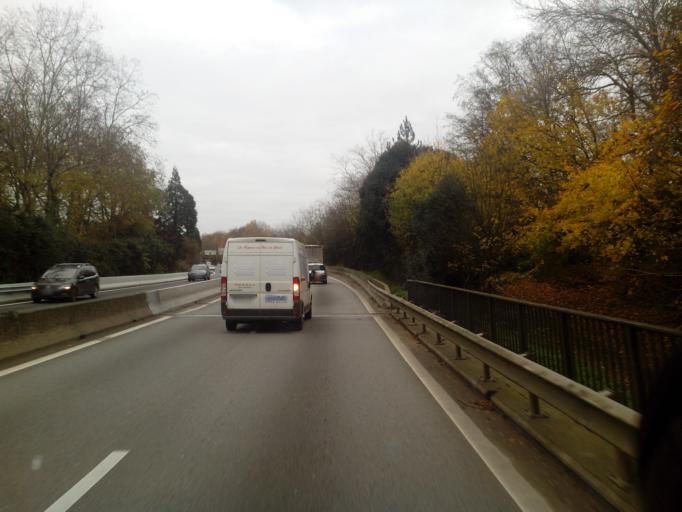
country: FR
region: Pays de la Loire
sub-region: Departement de la Loire-Atlantique
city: Nantes
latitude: 47.2558
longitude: -1.5379
